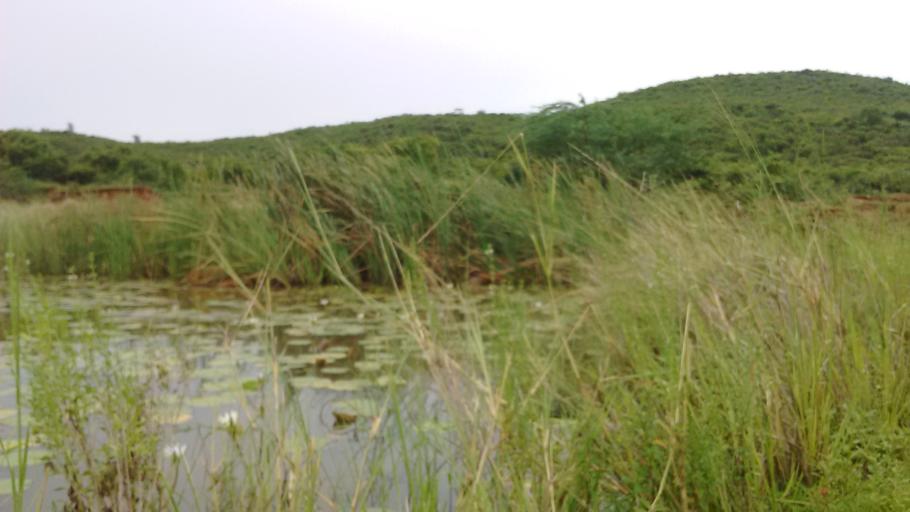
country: IN
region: Tamil Nadu
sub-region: Kancheepuram
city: Madambakkam
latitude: 12.9197
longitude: 80.0062
